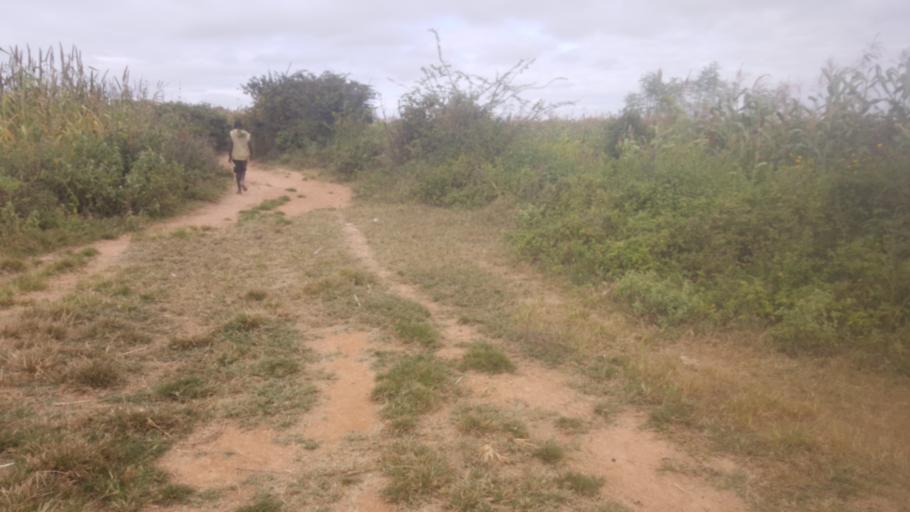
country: TZ
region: Dodoma
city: Msanga
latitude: -6.0408
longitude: 35.9389
